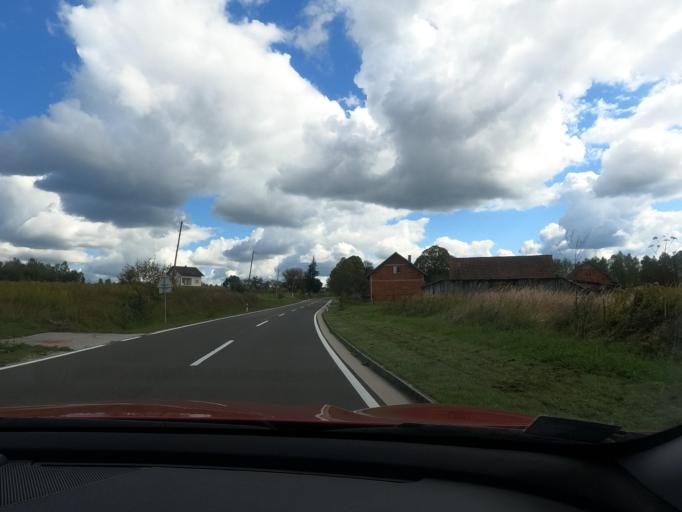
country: HR
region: Sisacko-Moslavacka
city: Gvozd
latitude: 45.3339
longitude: 15.9172
